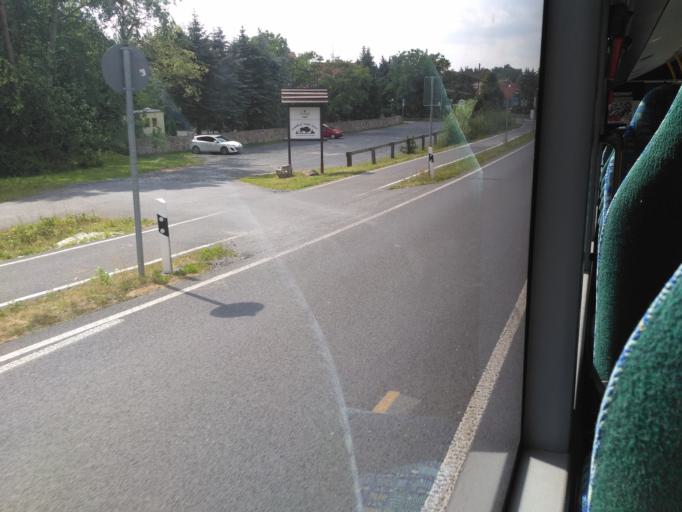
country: DE
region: Saxony
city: Moritzburg
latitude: 51.1596
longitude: 13.6337
